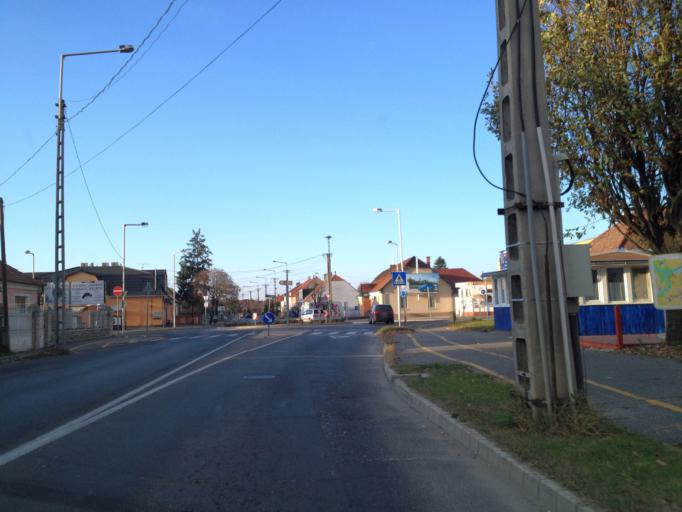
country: HU
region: Gyor-Moson-Sopron
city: Gyor
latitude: 47.6579
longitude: 17.6556
